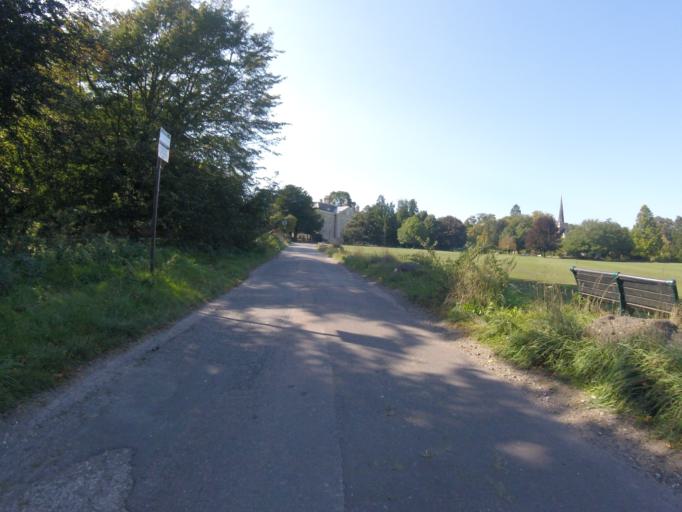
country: GB
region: England
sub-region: Brighton and Hove
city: Brighton
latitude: 50.8691
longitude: -0.1005
